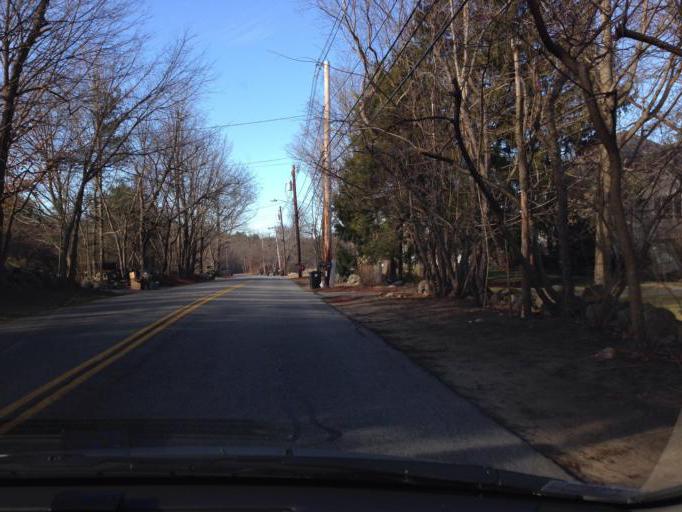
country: US
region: Massachusetts
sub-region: Middlesex County
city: Bedford
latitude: 42.4944
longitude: -71.3021
